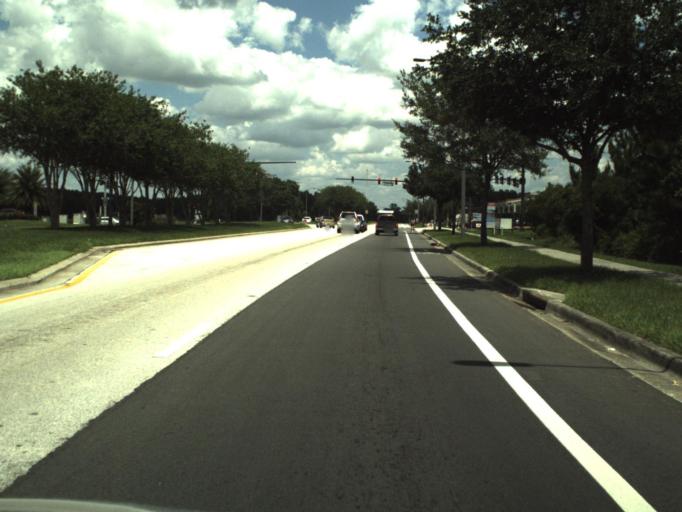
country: US
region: Florida
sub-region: Orange County
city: Conway
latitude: 28.4311
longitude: -81.2568
